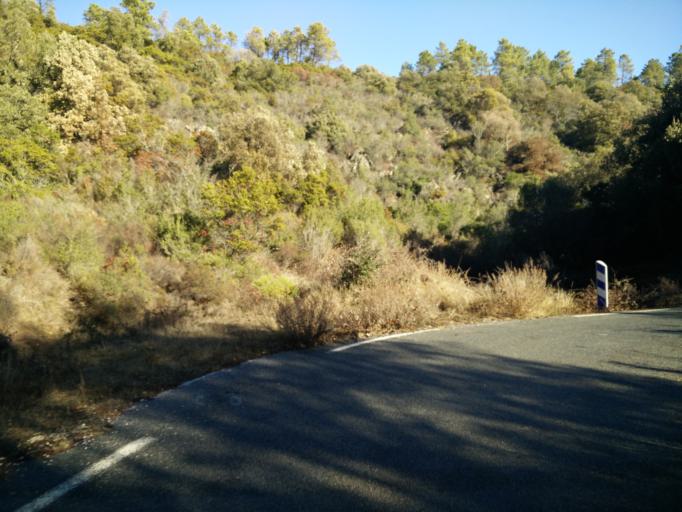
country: FR
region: Provence-Alpes-Cote d'Azur
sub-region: Departement du Var
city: Collobrieres
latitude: 43.2350
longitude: 6.3652
